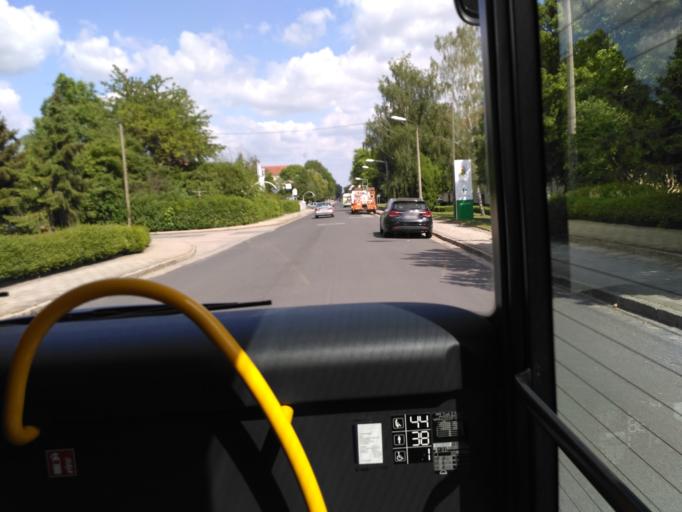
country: DE
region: Saxony
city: Riesa
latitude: 51.3197
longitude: 13.2547
